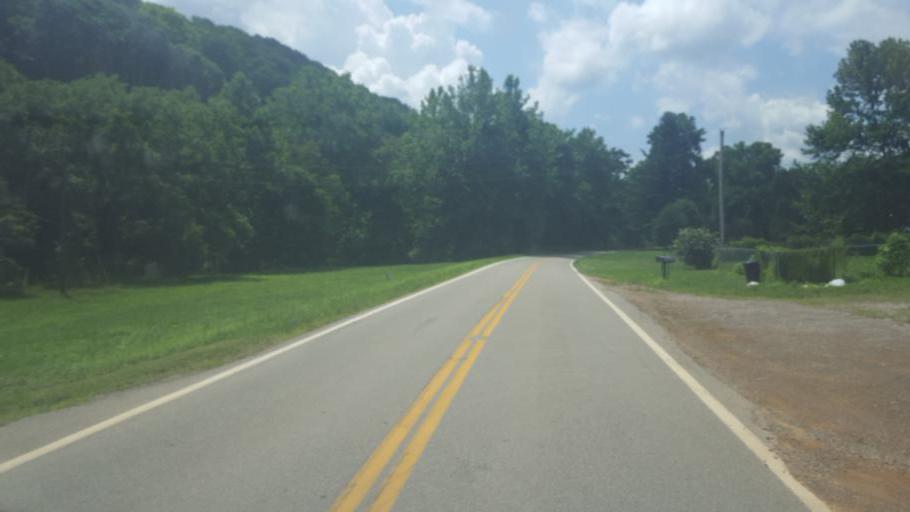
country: US
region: Ohio
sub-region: Ross County
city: Kingston
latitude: 39.3861
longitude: -82.7259
